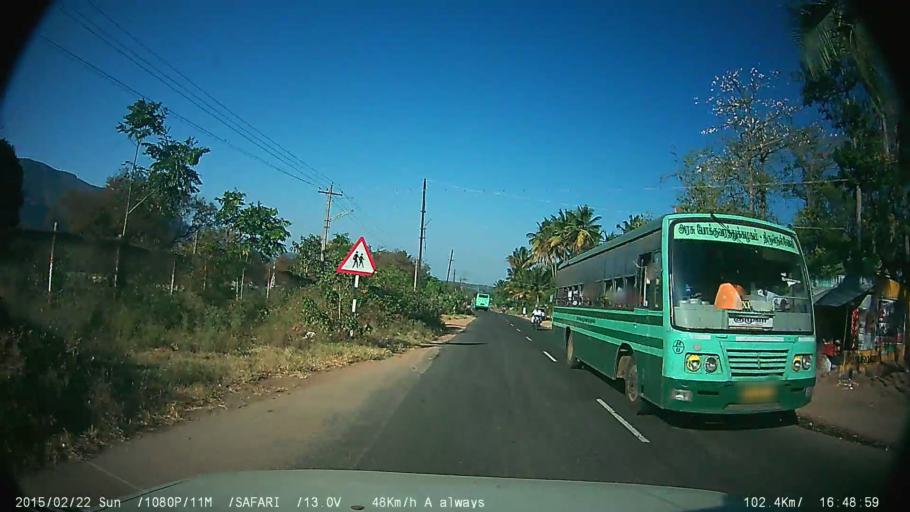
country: IN
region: Tamil Nadu
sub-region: Theni
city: Gudalur
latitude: 9.6288
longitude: 77.1984
